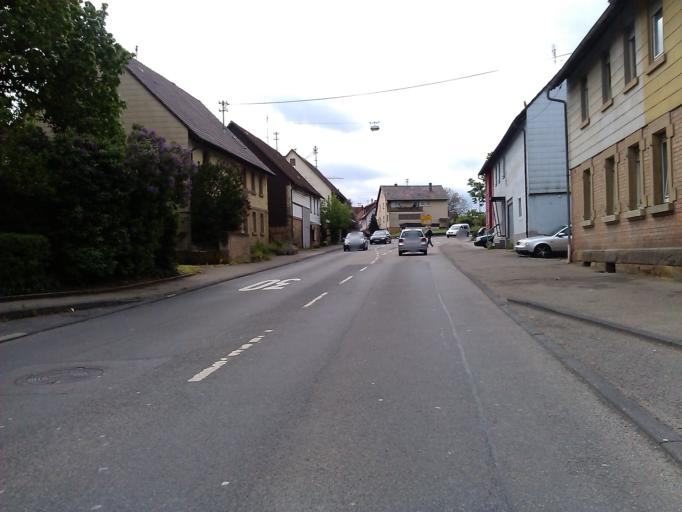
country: DE
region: Baden-Wuerttemberg
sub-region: Regierungsbezirk Stuttgart
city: Brackenheim
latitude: 49.0868
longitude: 9.0780
